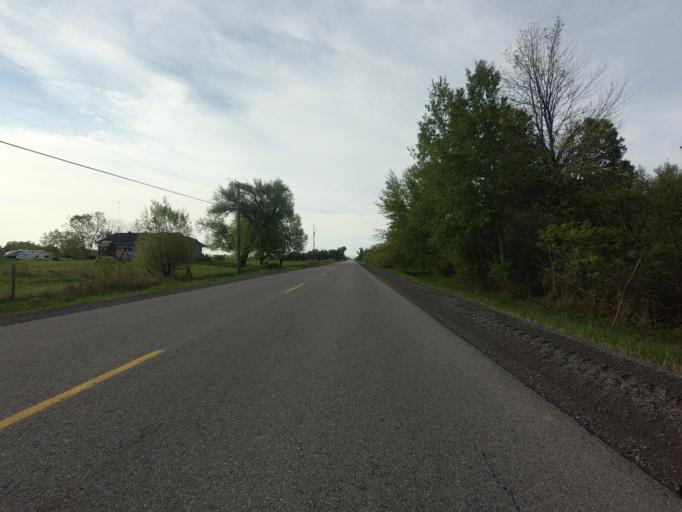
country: CA
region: Ontario
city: Ottawa
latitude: 45.3146
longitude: -75.4616
